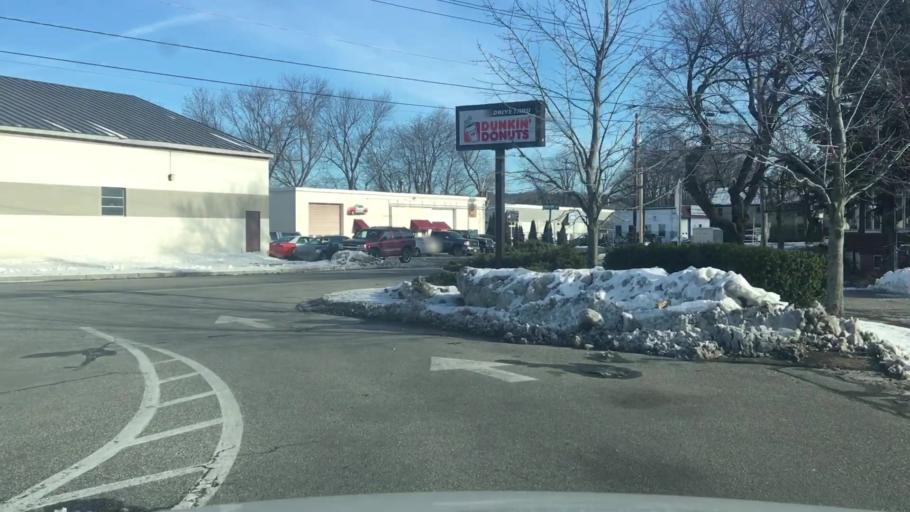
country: US
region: Maine
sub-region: Androscoggin County
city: Auburn
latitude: 44.0878
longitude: -70.2216
